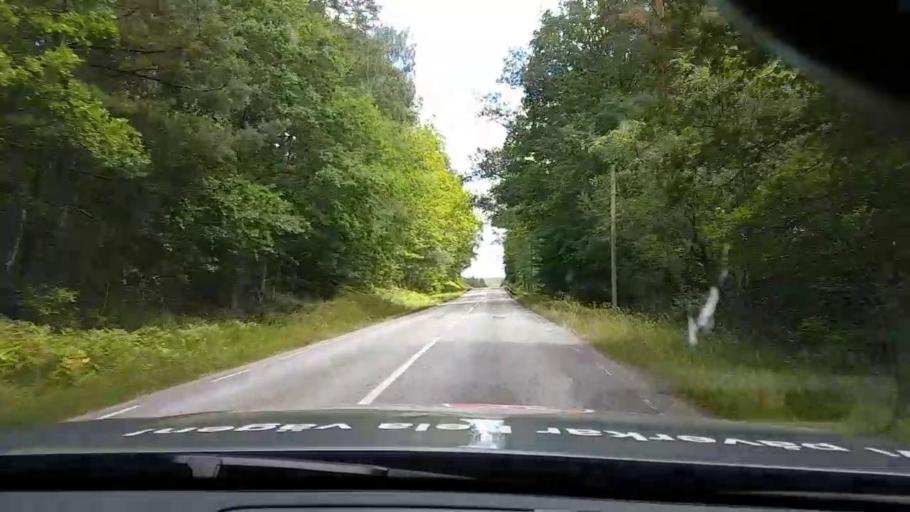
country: SE
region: Kalmar
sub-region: Vasterviks Kommun
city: Forserum
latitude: 58.0388
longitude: 16.4376
